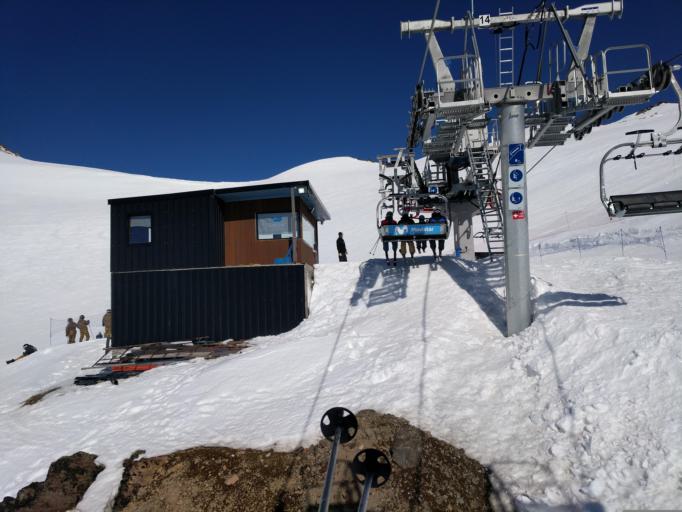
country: AR
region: Rio Negro
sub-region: Departamento de Bariloche
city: San Carlos de Bariloche
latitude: -41.1731
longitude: -71.4837
